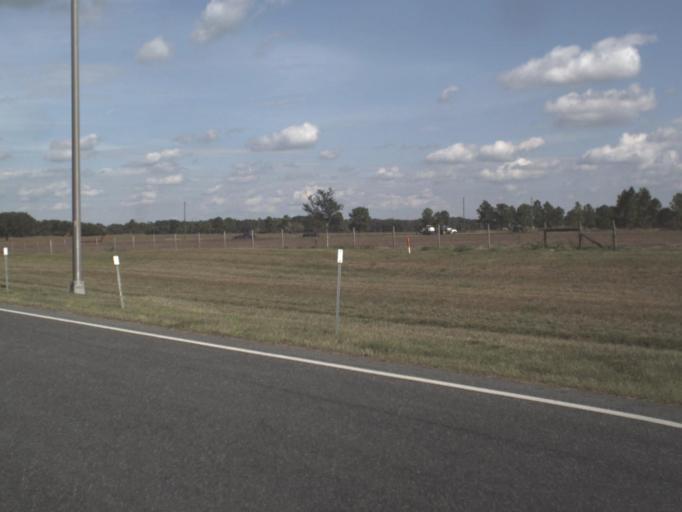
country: US
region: Florida
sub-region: Polk County
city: Auburndale
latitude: 28.1118
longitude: -81.8325
